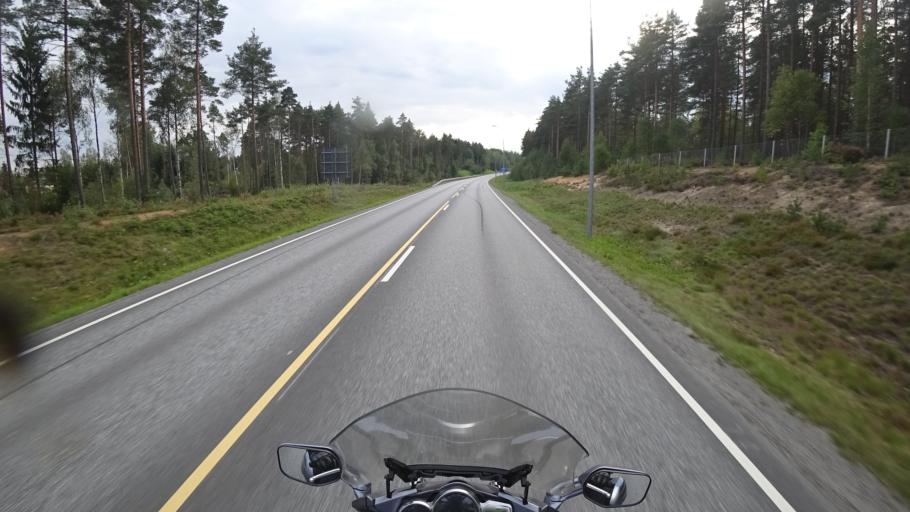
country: FI
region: Uusimaa
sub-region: Raaseporin
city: Karis
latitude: 60.0729
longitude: 23.6494
